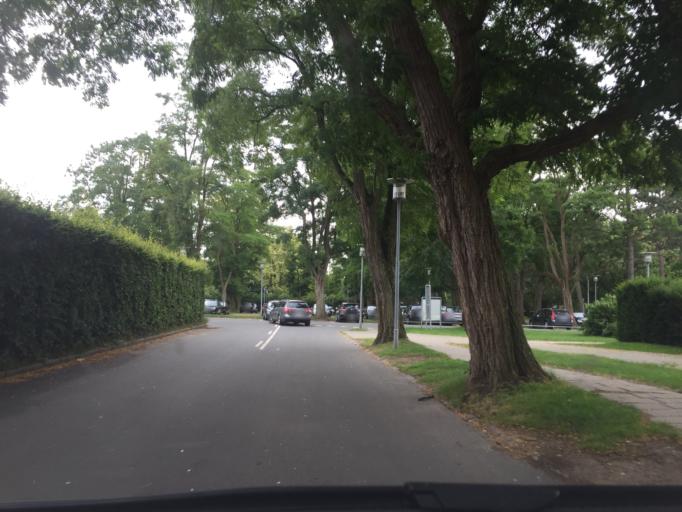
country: DK
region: Capital Region
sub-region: Lyngby-Tarbaek Kommune
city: Kongens Lyngby
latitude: 55.7807
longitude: 12.5076
